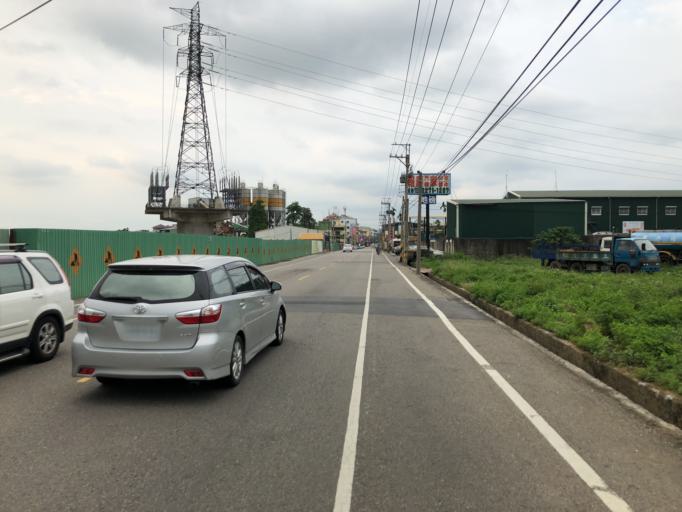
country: TW
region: Taiwan
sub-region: Taichung City
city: Taichung
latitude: 24.0990
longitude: 120.7289
